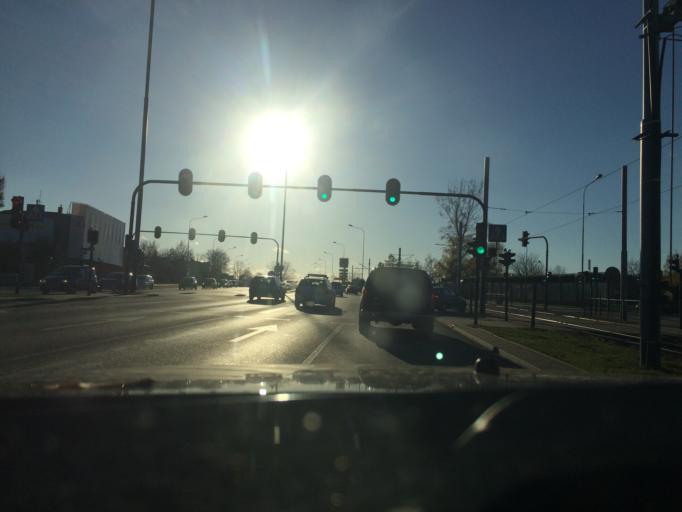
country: PL
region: Lodz Voivodeship
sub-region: Powiat pabianicki
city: Ksawerow
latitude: 51.7066
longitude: 19.4230
